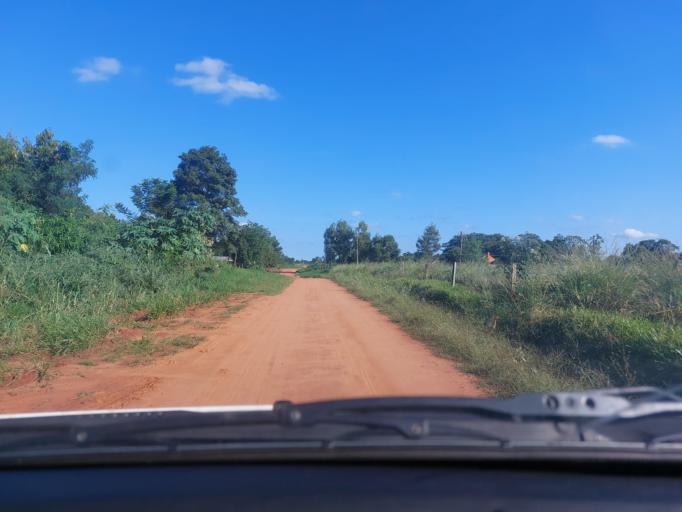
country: PY
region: San Pedro
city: Guayaybi
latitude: -24.5122
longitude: -56.5462
